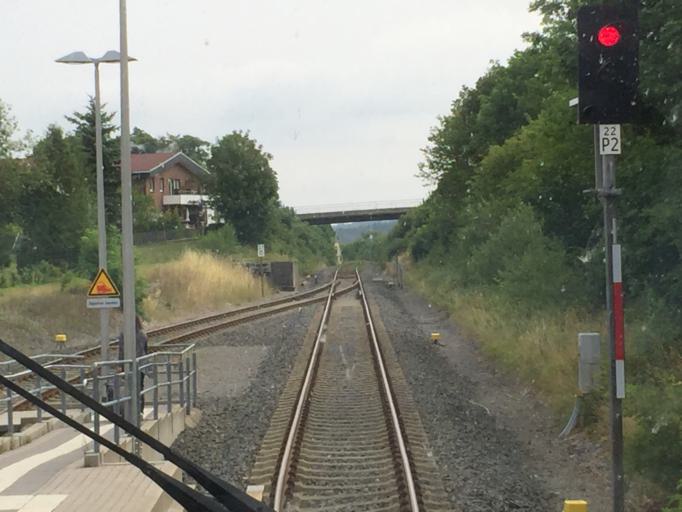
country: DE
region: Hesse
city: Willingen
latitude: 51.2806
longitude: 8.6701
